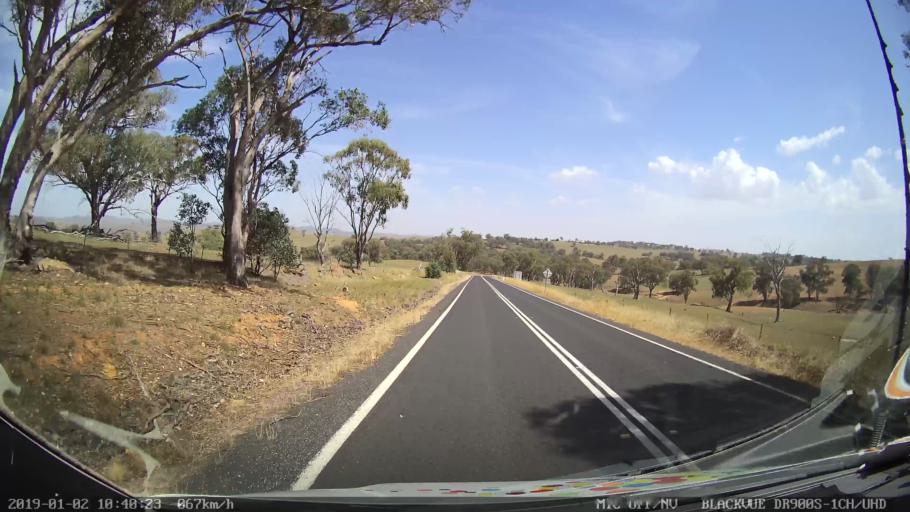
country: AU
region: New South Wales
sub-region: Cootamundra
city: Cootamundra
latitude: -34.8024
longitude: 148.3162
